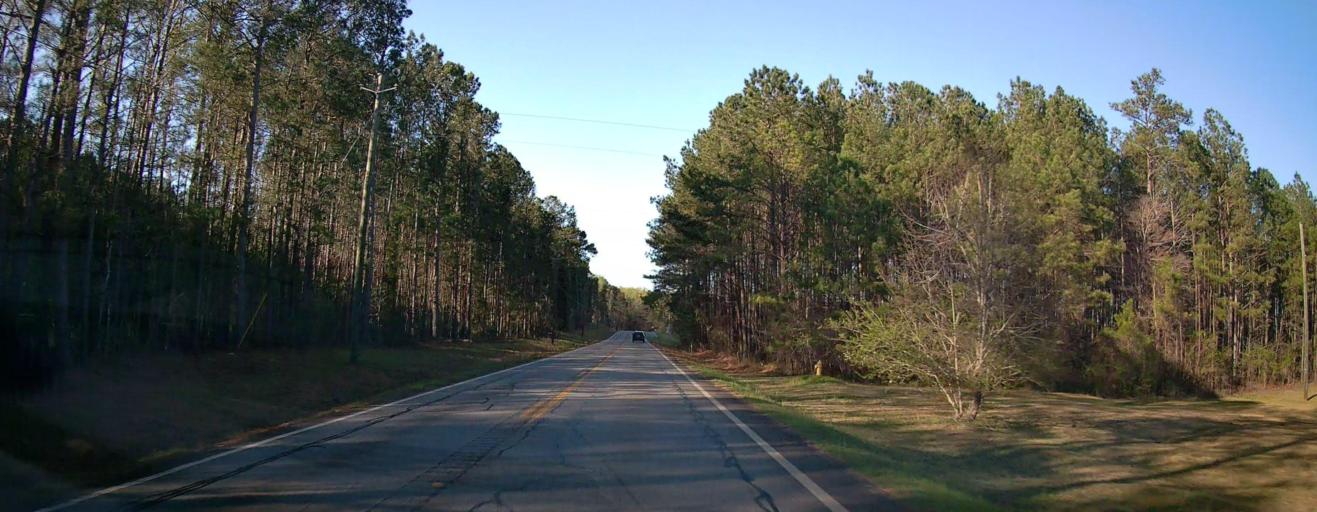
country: US
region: Georgia
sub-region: Butts County
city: Indian Springs
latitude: 33.2268
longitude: -83.9275
